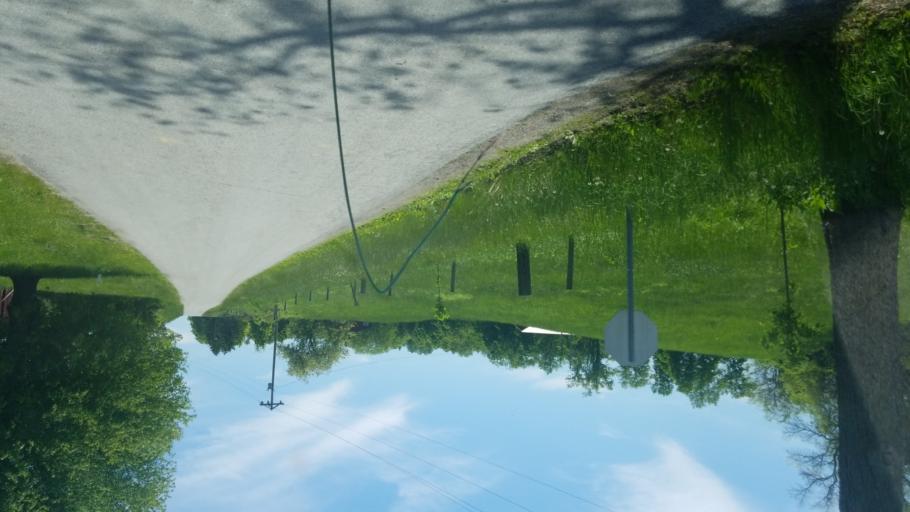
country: US
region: Ohio
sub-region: Huron County
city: Willard
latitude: 41.1200
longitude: -82.6860
